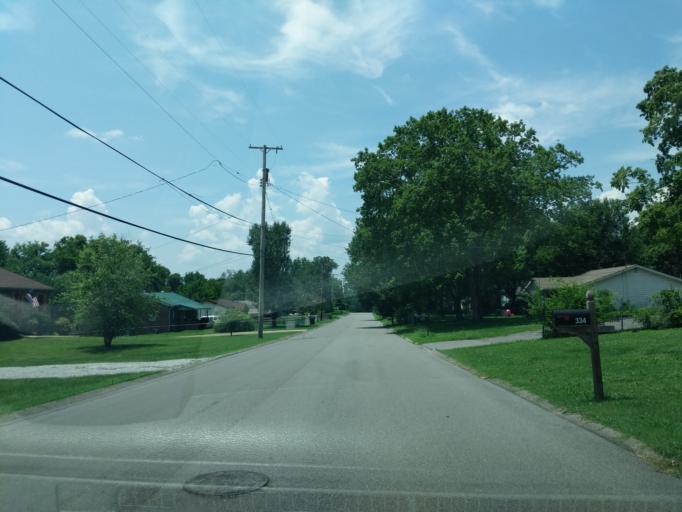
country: US
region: Tennessee
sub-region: Davidson County
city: Lakewood
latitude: 36.2375
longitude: -86.6323
